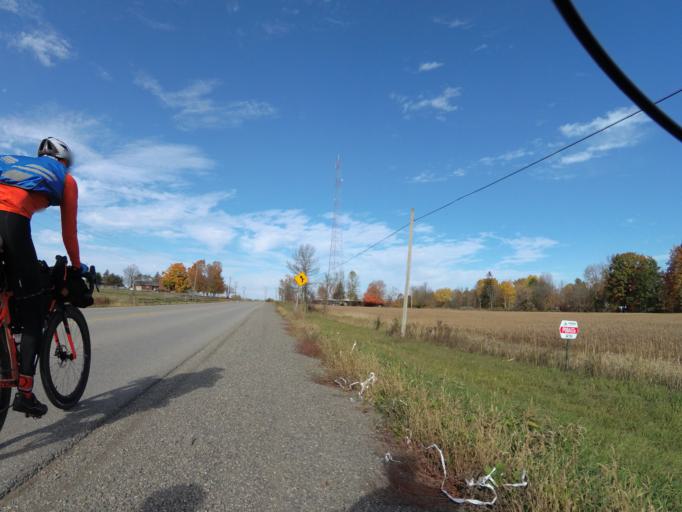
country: CA
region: Ontario
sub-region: Lanark County
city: Smiths Falls
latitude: 44.8899
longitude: -76.0097
